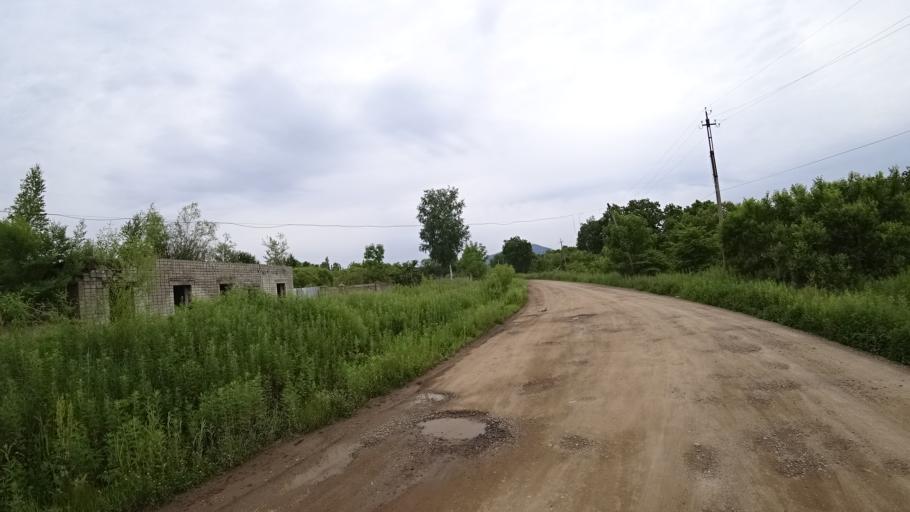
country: RU
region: Primorskiy
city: Arsen'yev
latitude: 44.1972
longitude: 133.3075
